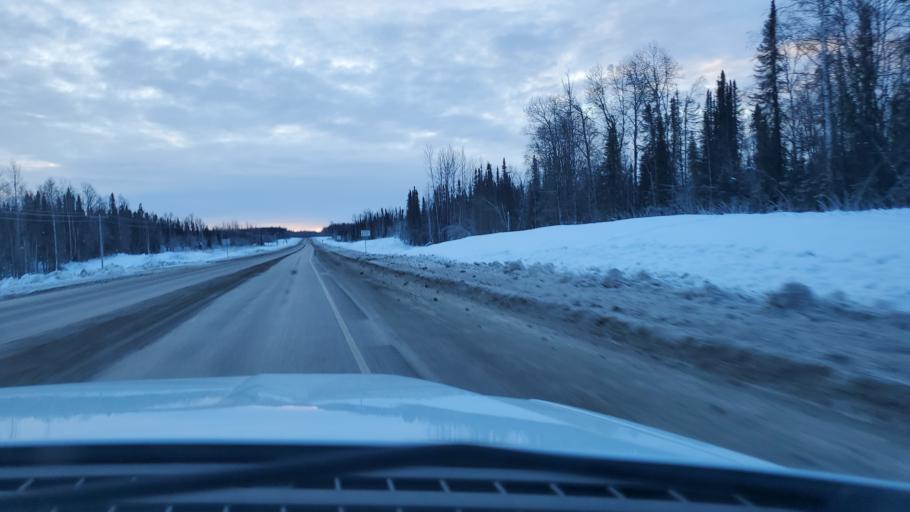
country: US
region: Alaska
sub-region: Matanuska-Susitna Borough
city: Y
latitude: 62.1285
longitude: -150.0406
